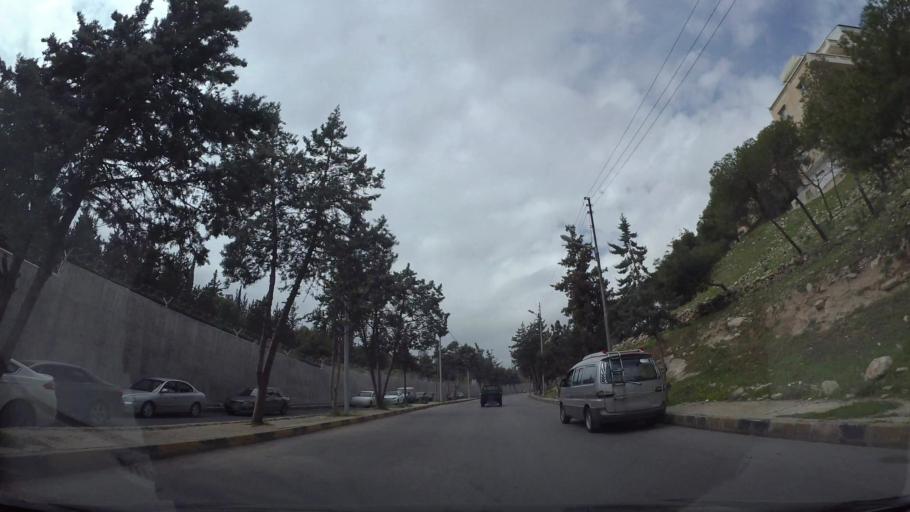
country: JO
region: Amman
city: Amman
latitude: 31.9602
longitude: 35.9526
